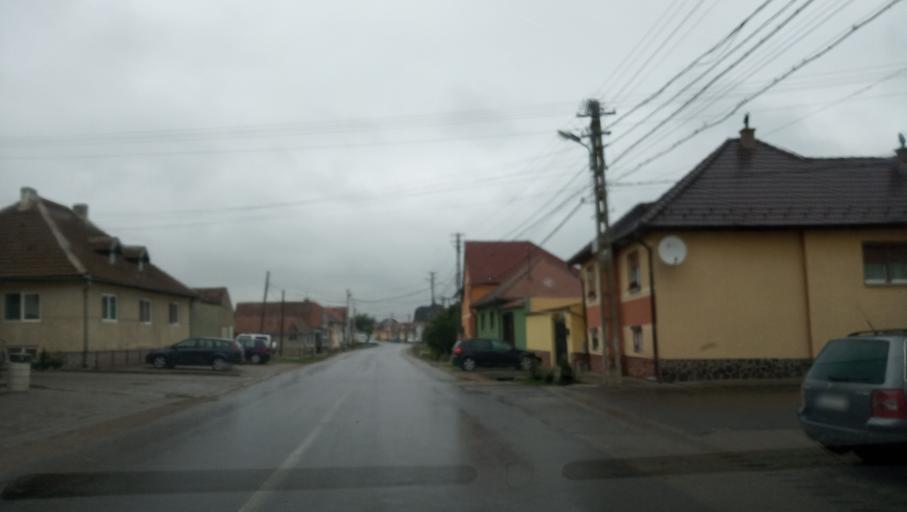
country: RO
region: Sibiu
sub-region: Comuna Selimbar
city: Vestem
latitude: 45.7171
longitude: 24.2382
